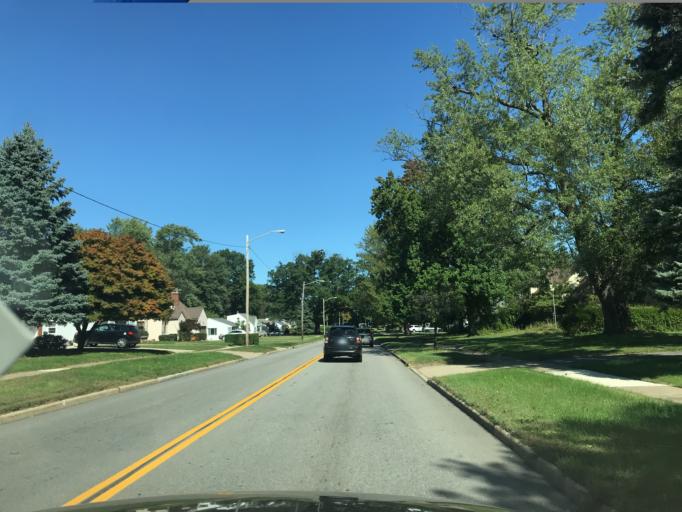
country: US
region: Ohio
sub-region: Lake County
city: Kirtland
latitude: 41.6483
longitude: -81.3756
